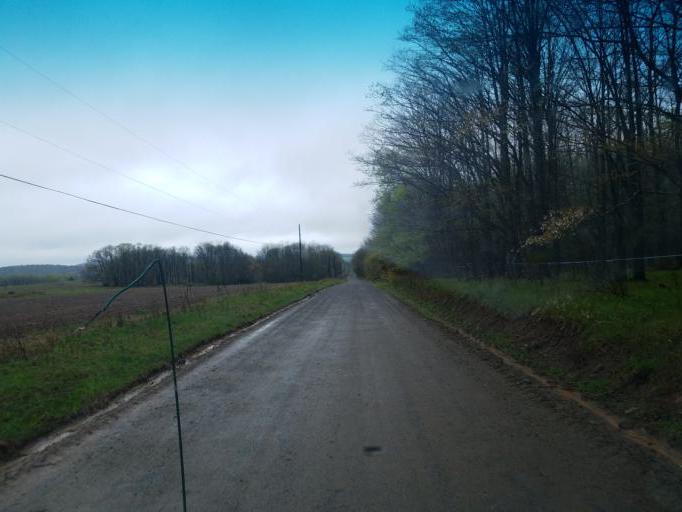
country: US
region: New York
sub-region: Allegany County
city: Andover
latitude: 41.9891
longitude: -77.7309
